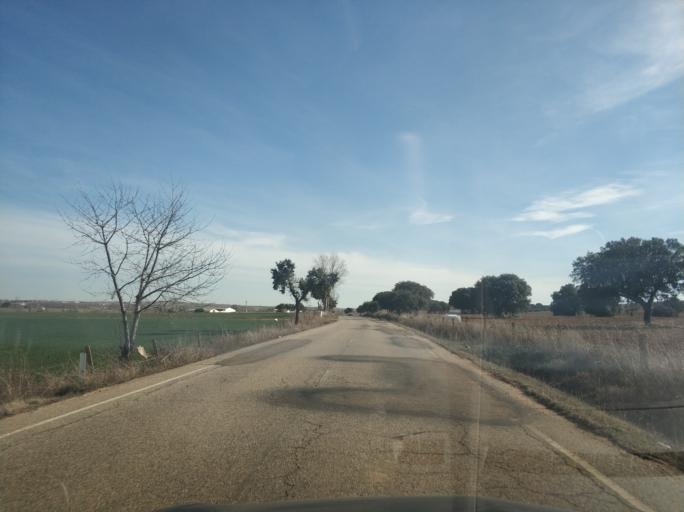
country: ES
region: Castille and Leon
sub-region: Provincia de Salamanca
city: Florida de Liebana
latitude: 41.0145
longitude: -5.7413
